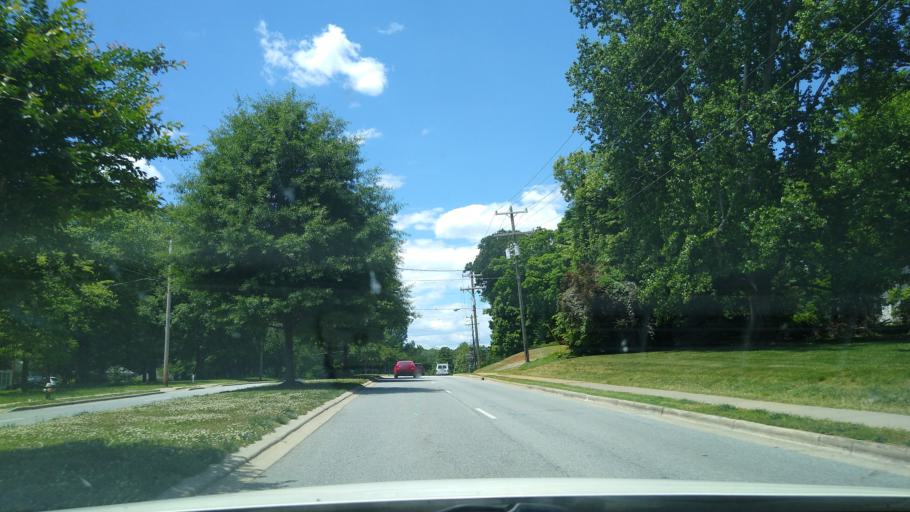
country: US
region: North Carolina
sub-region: Guilford County
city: Greensboro
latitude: 36.0885
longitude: -79.8489
